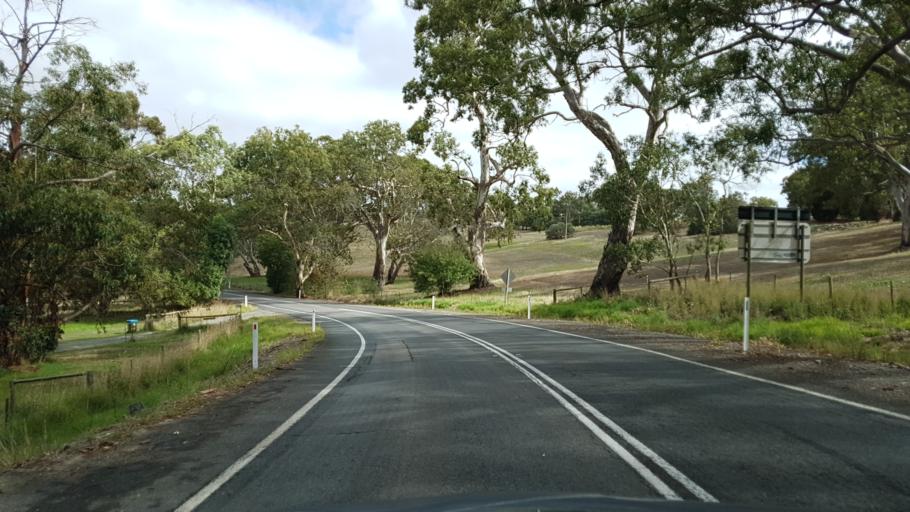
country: AU
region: South Australia
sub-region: Mount Barker
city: Nairne
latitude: -35.0399
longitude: 138.9253
